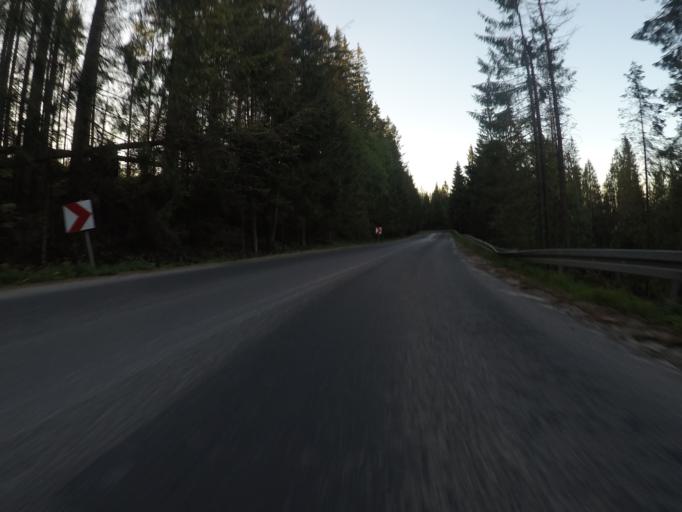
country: PL
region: Lesser Poland Voivodeship
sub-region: Powiat tatrzanski
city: Poronin
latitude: 49.2866
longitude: 20.0258
